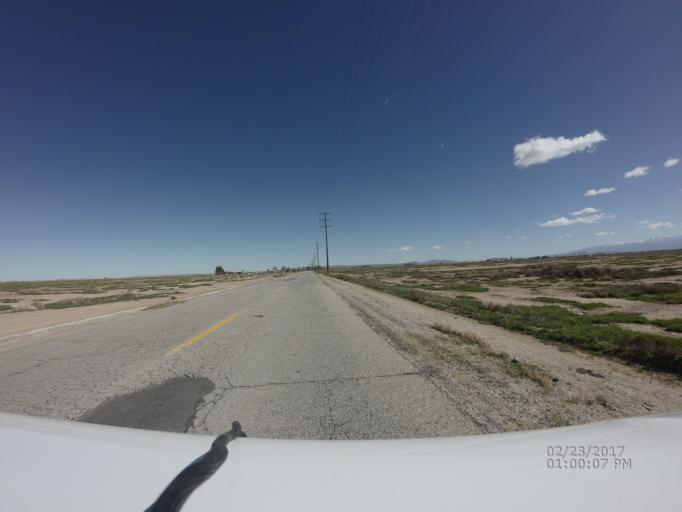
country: US
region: California
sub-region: Los Angeles County
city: Lancaster
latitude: 34.7630
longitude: -118.0294
